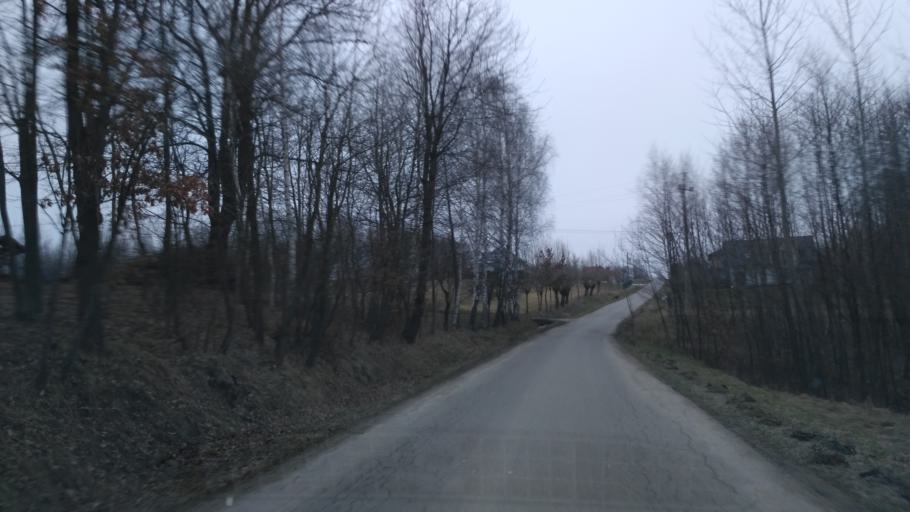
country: PL
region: Subcarpathian Voivodeship
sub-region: Powiat rzeszowski
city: Chmielnik
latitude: 49.9777
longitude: 22.1457
